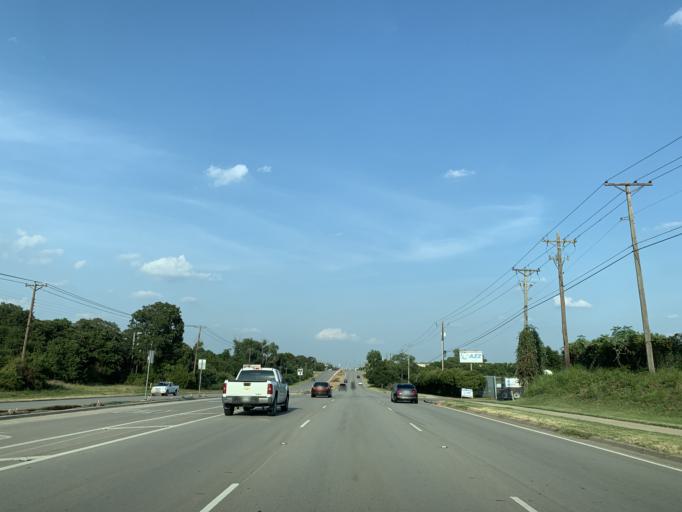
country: US
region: Texas
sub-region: Tarrant County
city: Hurst
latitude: 32.8090
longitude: -97.1815
